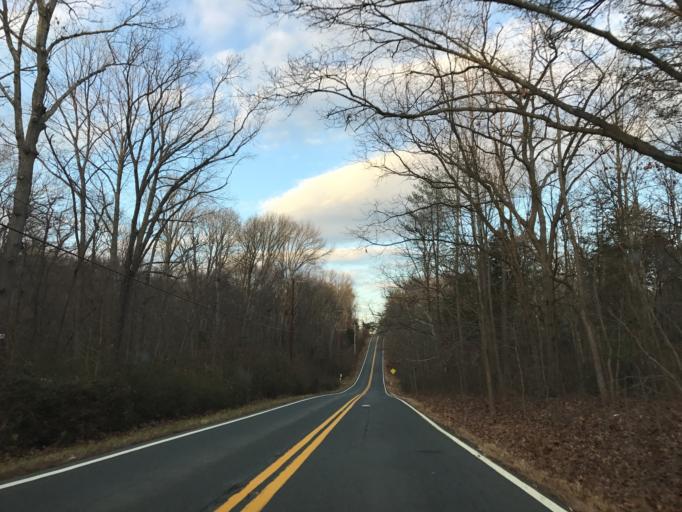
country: US
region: Maryland
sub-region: Cecil County
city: Charlestown
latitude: 39.4949
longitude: -75.9723
